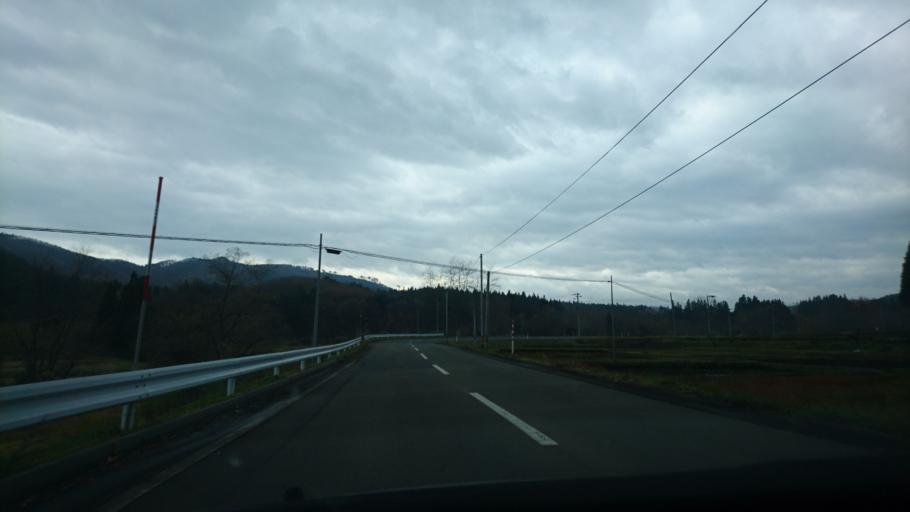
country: JP
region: Iwate
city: Ichinoseki
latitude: 38.9548
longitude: 140.9351
